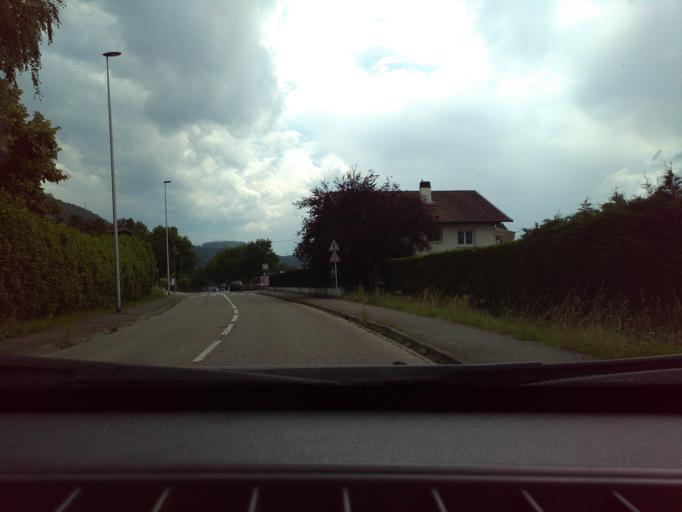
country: FR
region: Rhone-Alpes
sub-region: Departement de l'Isere
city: Saint-Martin-d'Heres
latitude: 45.1725
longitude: 5.7689
